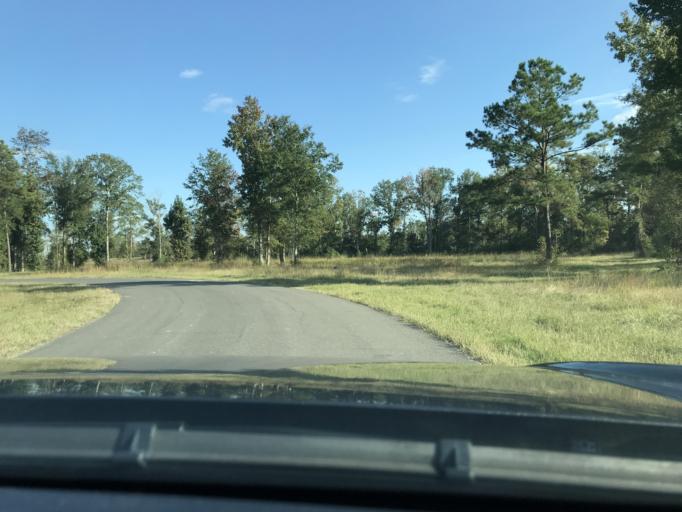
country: US
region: Louisiana
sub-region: Calcasieu Parish
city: Moss Bluff
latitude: 30.3318
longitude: -93.2490
